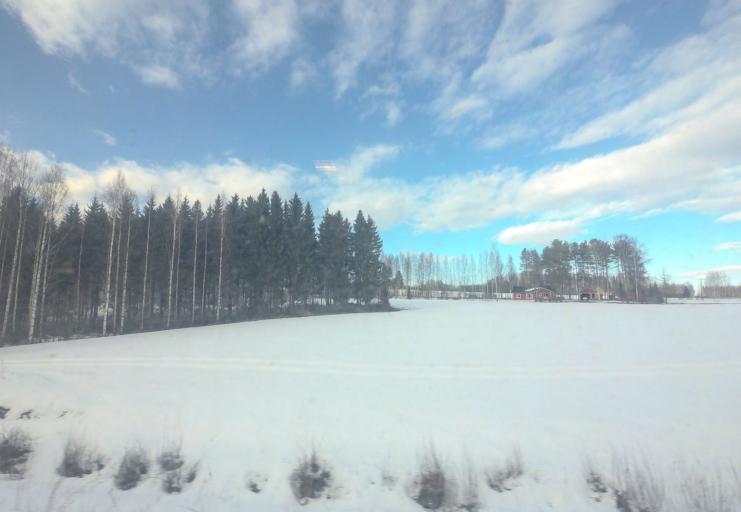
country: FI
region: Southern Savonia
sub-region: Savonlinna
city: Kerimaeki
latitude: 61.8341
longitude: 29.1918
